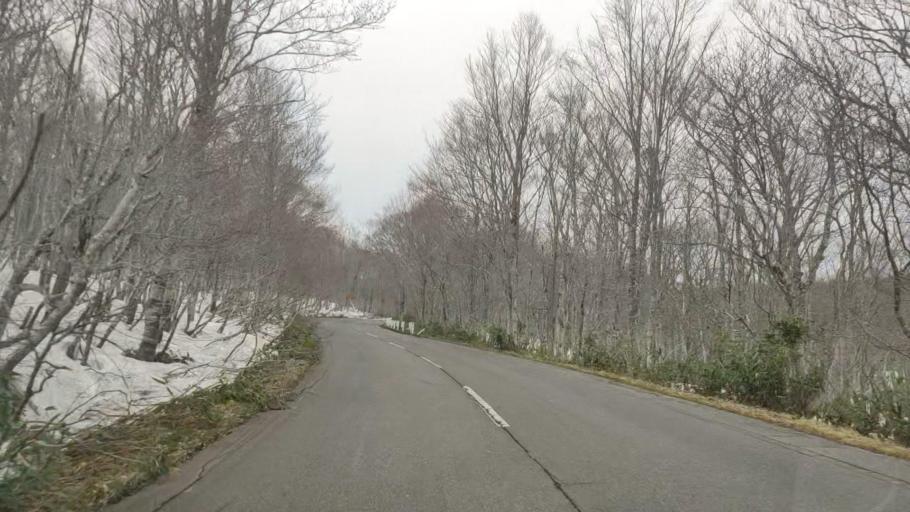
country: JP
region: Aomori
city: Aomori Shi
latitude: 40.6501
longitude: 140.9459
